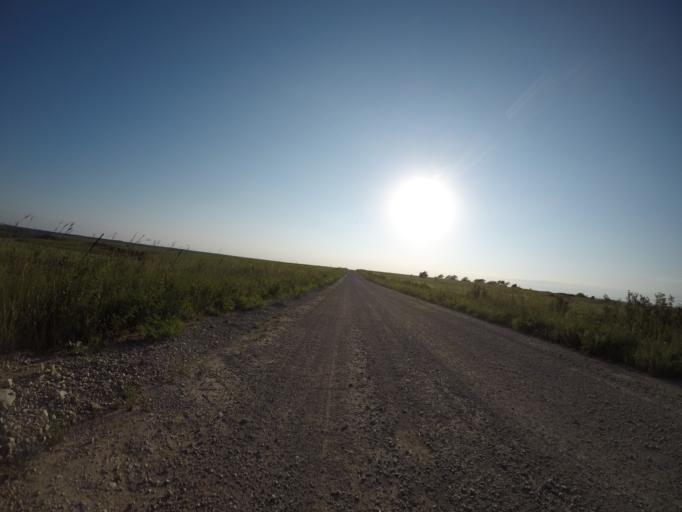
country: US
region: Kansas
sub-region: Riley County
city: Ogden
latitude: 39.0485
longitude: -96.6891
